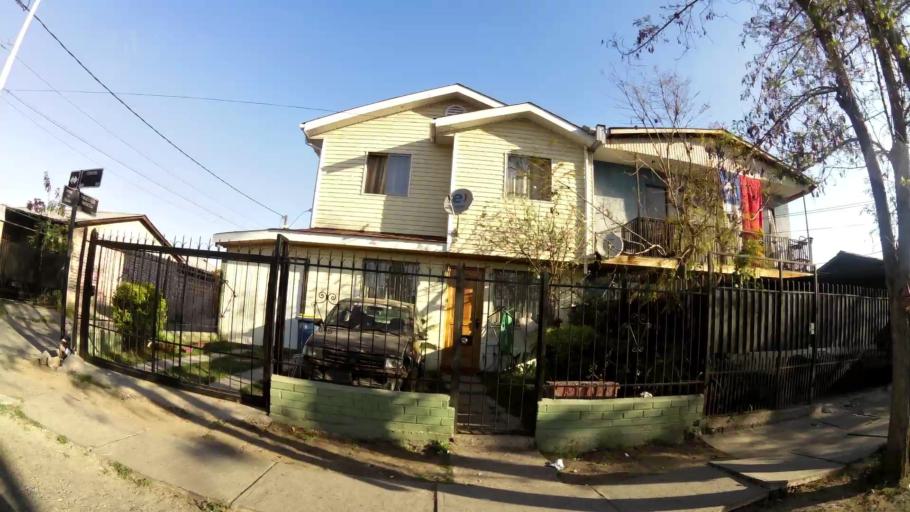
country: CL
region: Santiago Metropolitan
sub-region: Provincia de Santiago
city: La Pintana
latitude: -33.5530
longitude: -70.6233
